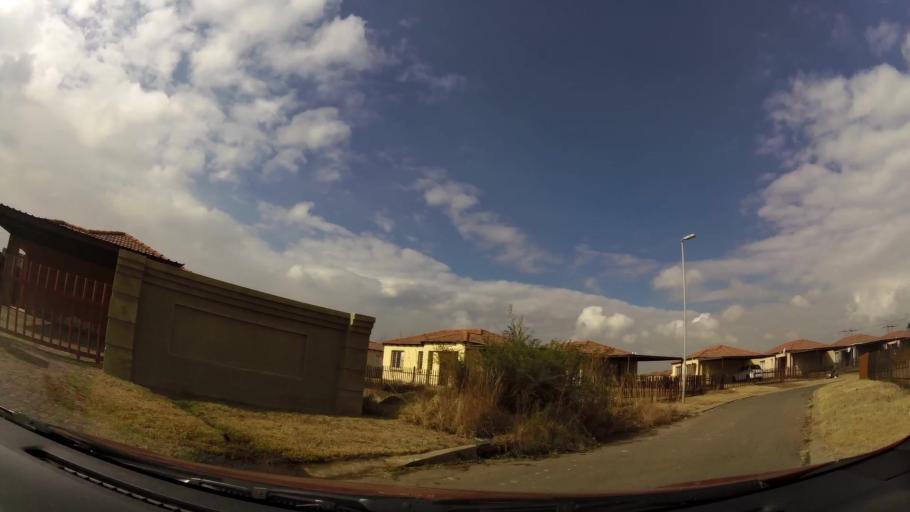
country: ZA
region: Gauteng
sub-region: Sedibeng District Municipality
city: Vanderbijlpark
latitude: -26.7153
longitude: 27.8814
